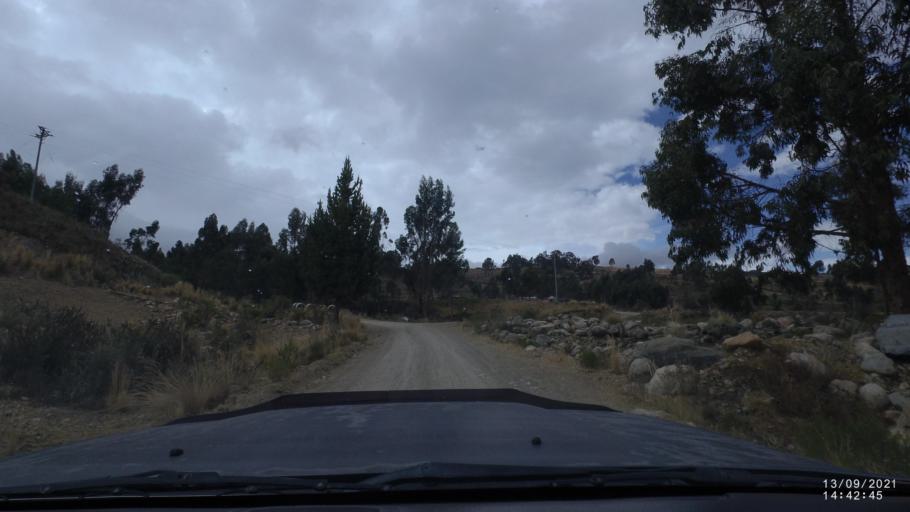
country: BO
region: Cochabamba
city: Colomi
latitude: -17.3617
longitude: -65.8136
